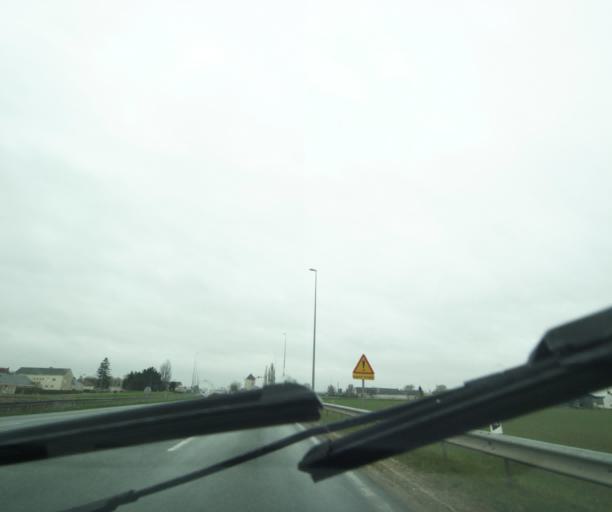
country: FR
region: Centre
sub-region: Departement du Loiret
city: Artenay
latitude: 48.0852
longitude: 1.8753
